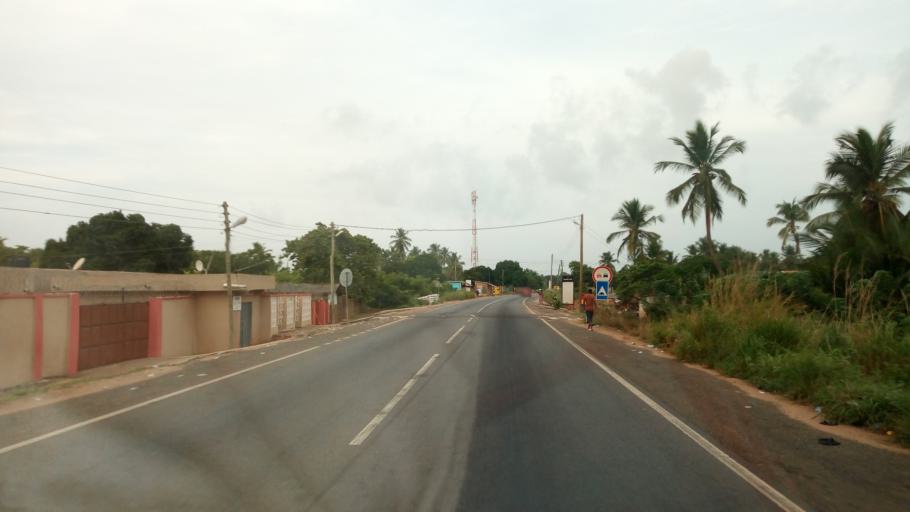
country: TG
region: Maritime
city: Lome
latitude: 6.0817
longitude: 1.0527
